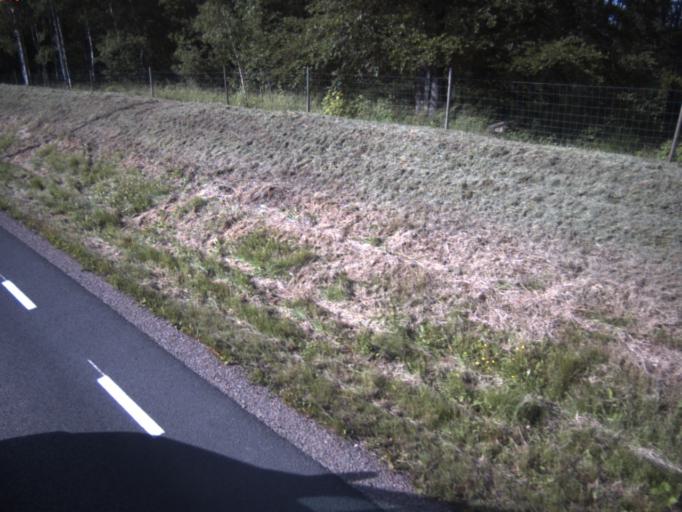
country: SE
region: Skane
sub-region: Helsingborg
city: Odakra
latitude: 56.0944
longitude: 12.7676
